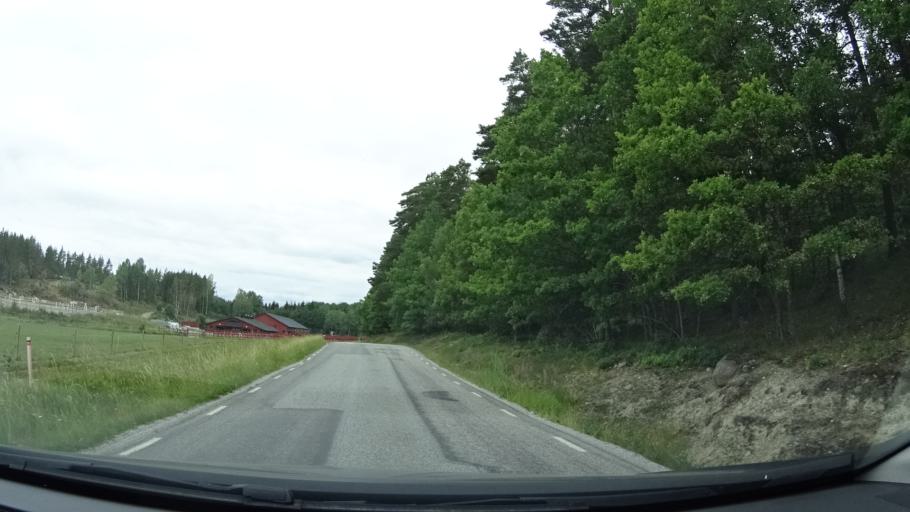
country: SE
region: Stockholm
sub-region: Varmdo Kommun
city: Hemmesta
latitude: 59.3605
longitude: 18.4845
